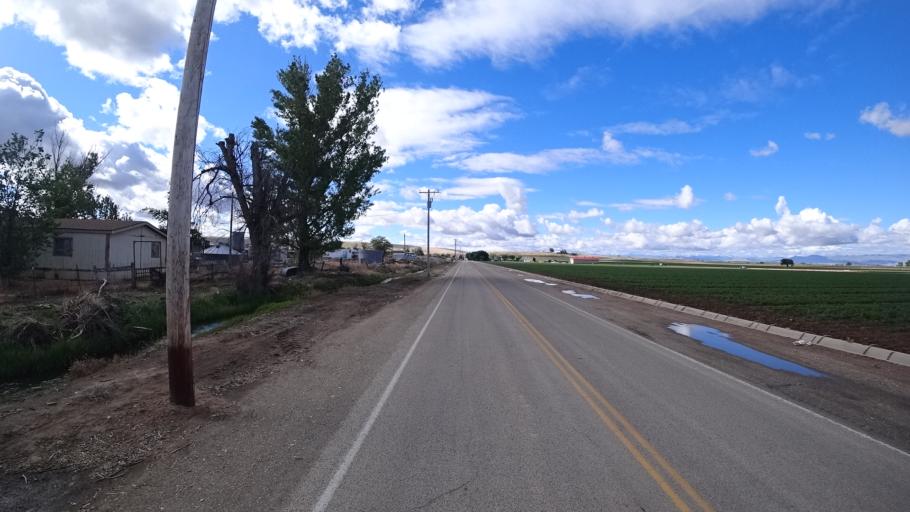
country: US
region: Idaho
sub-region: Ada County
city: Kuna
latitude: 43.4735
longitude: -116.4735
